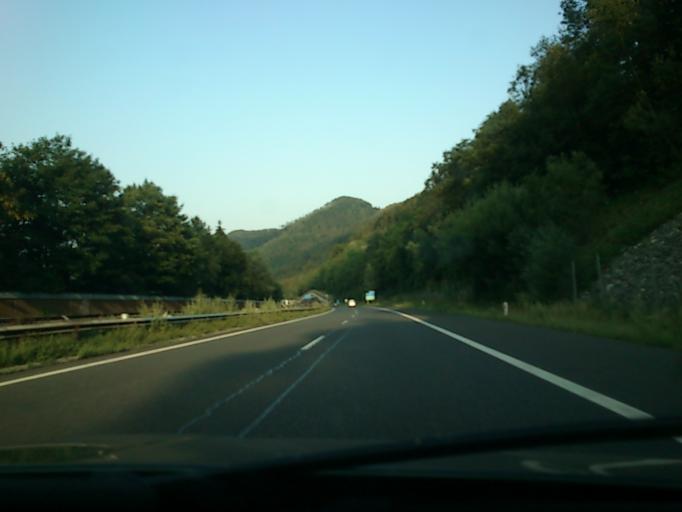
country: AT
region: Styria
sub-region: Politischer Bezirk Graz-Umgebung
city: Ubelbach
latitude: 47.2166
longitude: 15.2540
